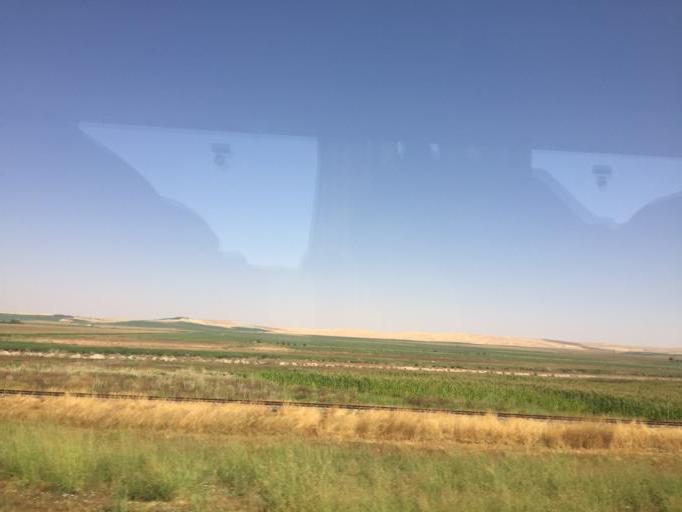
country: TR
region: Diyarbakir
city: Tepe
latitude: 37.8496
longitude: 40.7879
